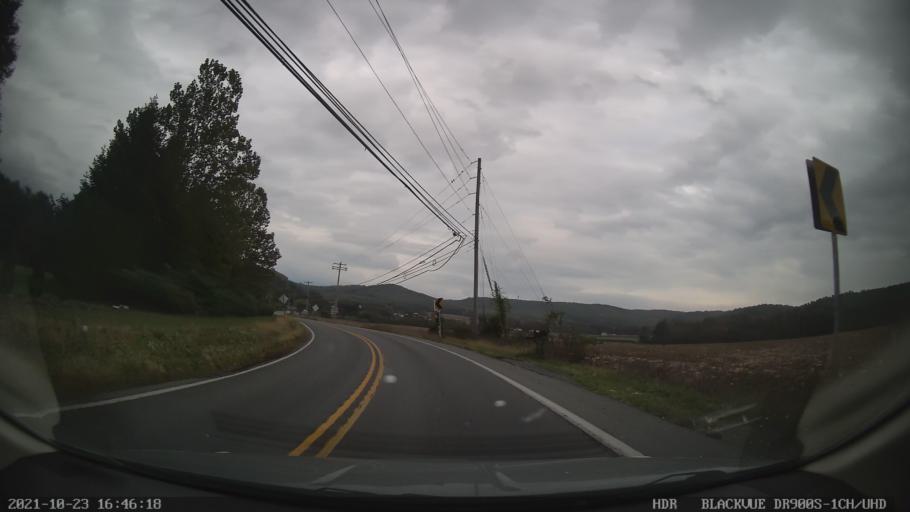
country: US
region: Pennsylvania
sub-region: Berks County
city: Red Lion
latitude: 40.4943
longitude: -75.6516
